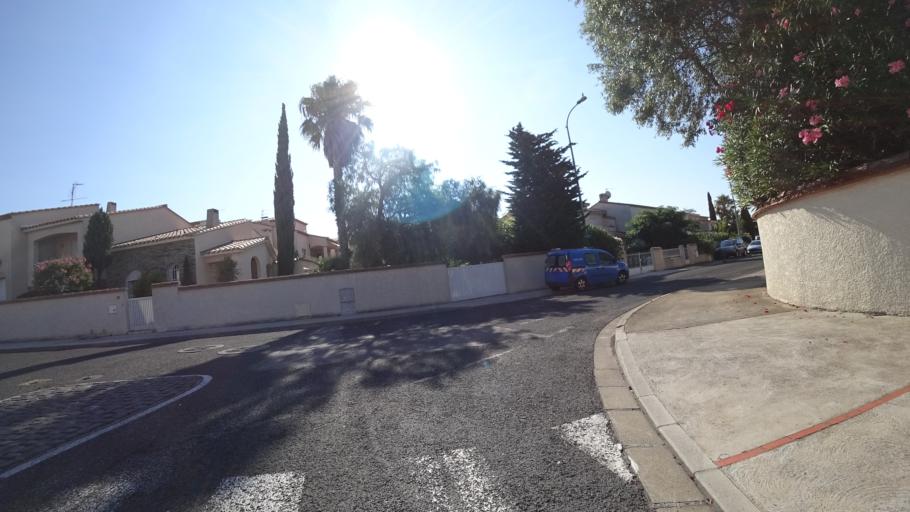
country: FR
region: Languedoc-Roussillon
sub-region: Departement des Pyrenees-Orientales
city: Cabestany
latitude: 42.6937
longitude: 2.9378
